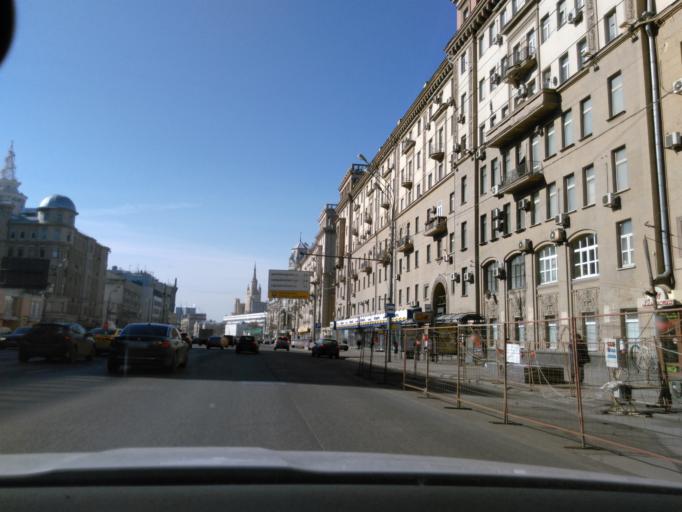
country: RU
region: Moscow
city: Moscow
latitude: 55.7676
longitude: 37.5928
